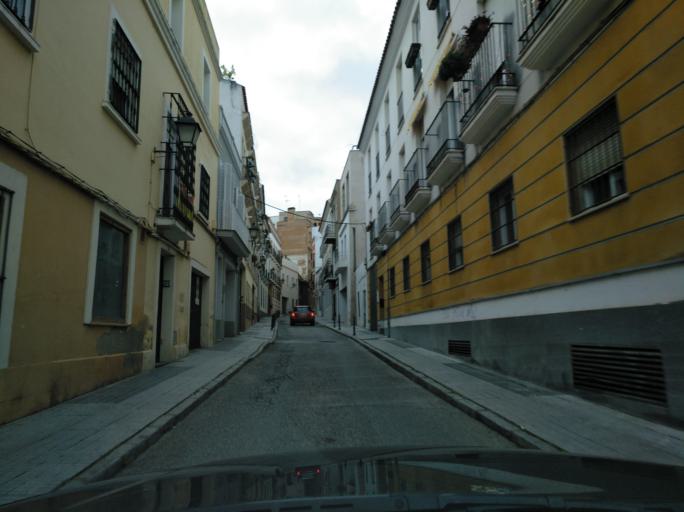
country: ES
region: Extremadura
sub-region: Provincia de Badajoz
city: Badajoz
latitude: 38.8785
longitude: -6.9653
